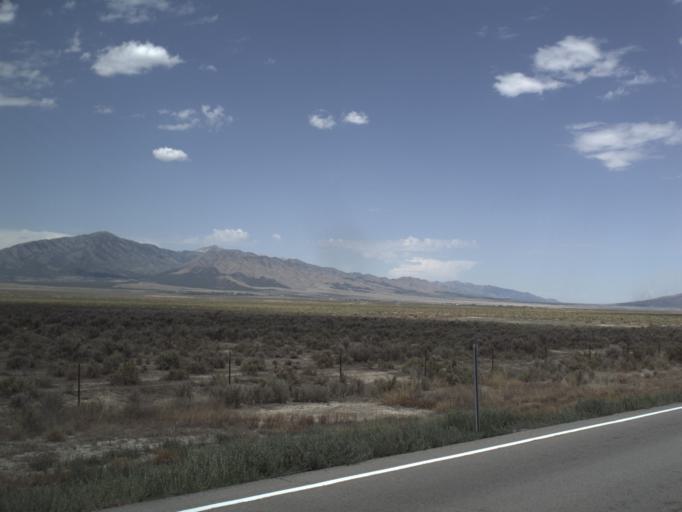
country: US
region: Utah
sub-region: Tooele County
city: Tooele
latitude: 40.2563
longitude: -112.3985
